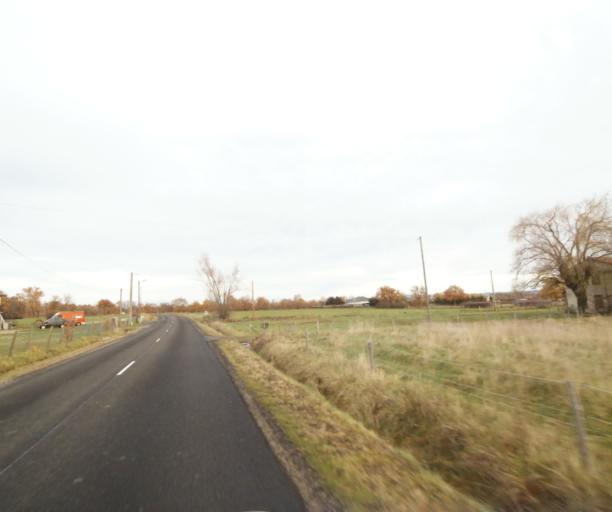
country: FR
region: Rhone-Alpes
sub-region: Departement de la Loire
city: Sury-le-Comtal
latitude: 45.5264
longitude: 4.1596
